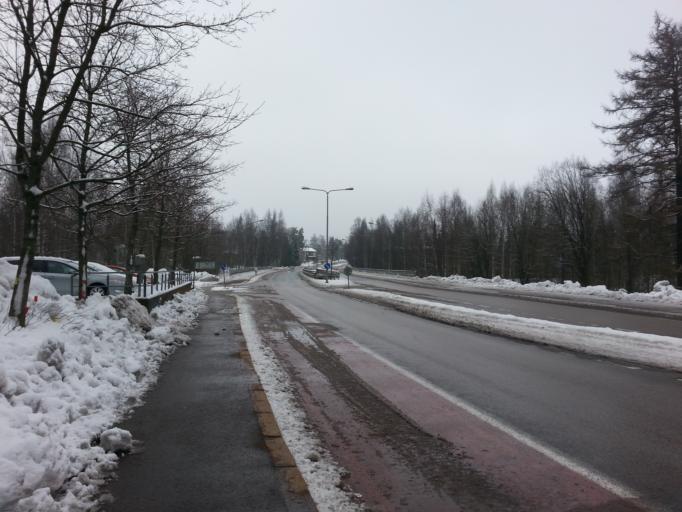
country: FI
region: Uusimaa
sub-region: Helsinki
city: Teekkarikylae
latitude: 60.2294
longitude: 24.8478
